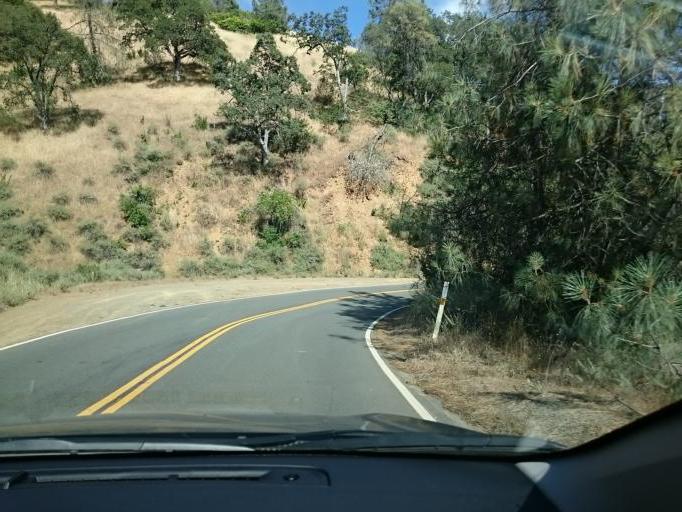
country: US
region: California
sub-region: Santa Clara County
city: East Foothills
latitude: 37.3394
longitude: -121.6669
